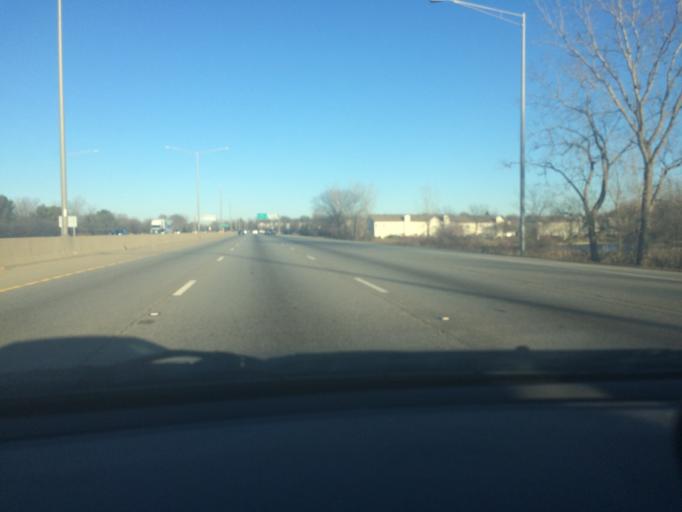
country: US
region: Illinois
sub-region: Cook County
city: Rolling Meadows
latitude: 42.1032
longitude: -88.0131
